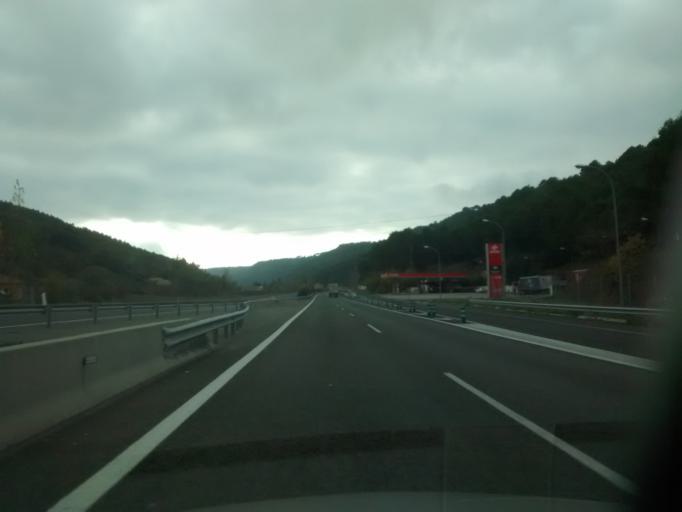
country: ES
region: Castille-La Mancha
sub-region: Provincia de Guadalajara
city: Torija
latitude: 40.7295
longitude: -3.0470
